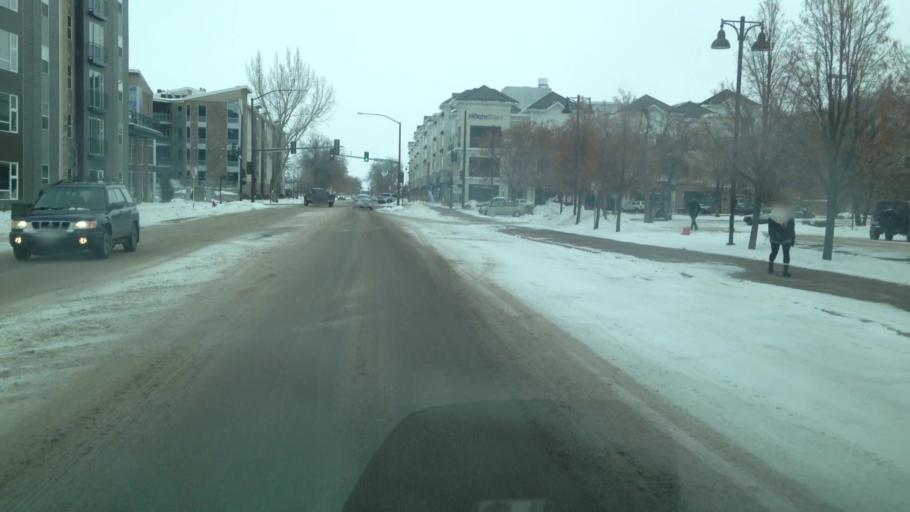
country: US
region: Idaho
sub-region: Madison County
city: Rexburg
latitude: 43.8208
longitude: -111.7867
